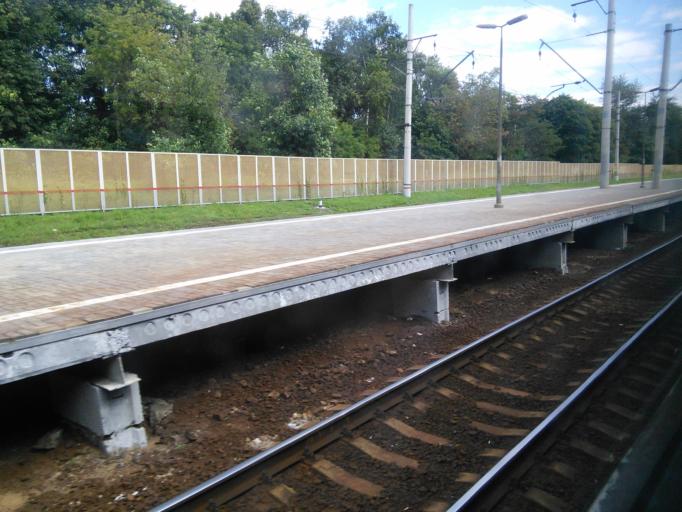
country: RU
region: Moscow
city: Zhulebino
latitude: 55.6999
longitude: 37.8617
